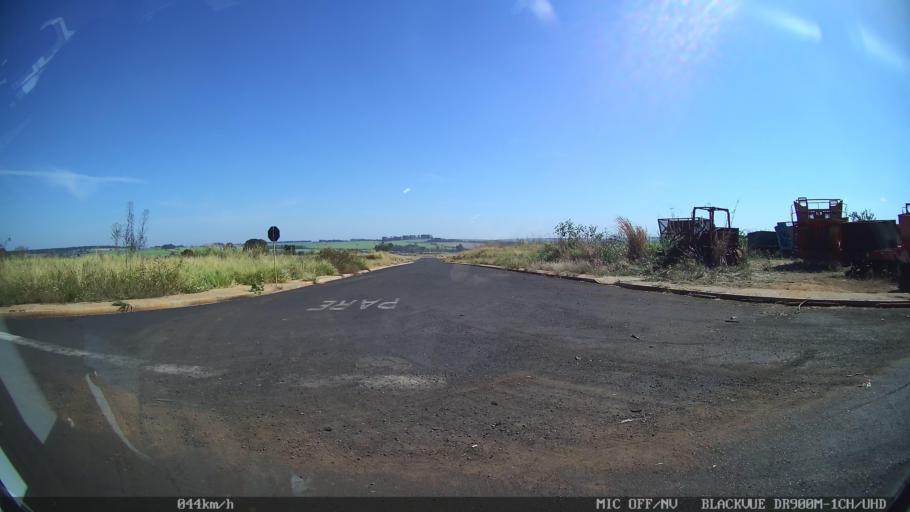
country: BR
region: Sao Paulo
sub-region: Batatais
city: Batatais
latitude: -20.8786
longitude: -47.6009
